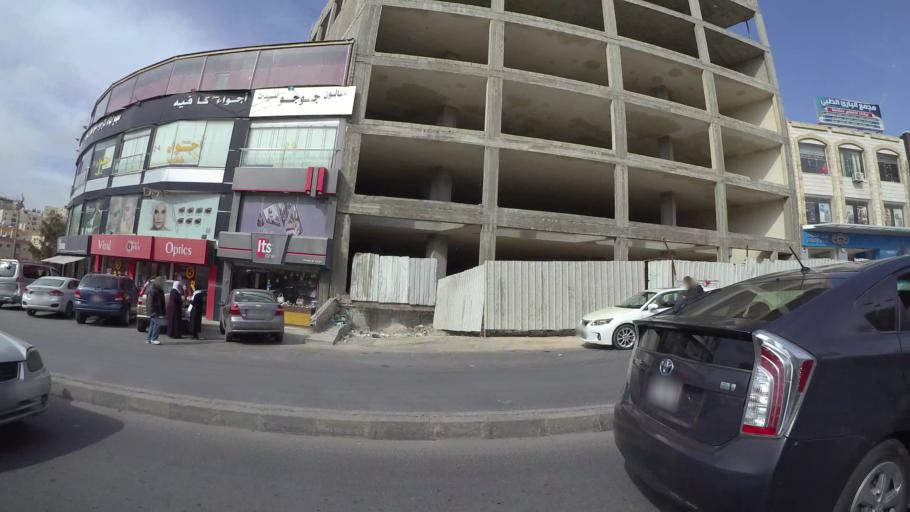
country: JO
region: Amman
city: Amman
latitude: 32.0033
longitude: 35.9368
